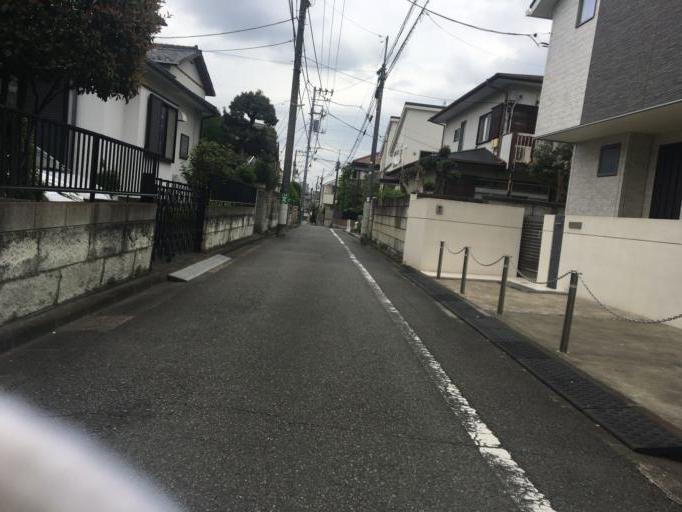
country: JP
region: Tokyo
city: Tokyo
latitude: 35.6724
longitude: 139.6318
